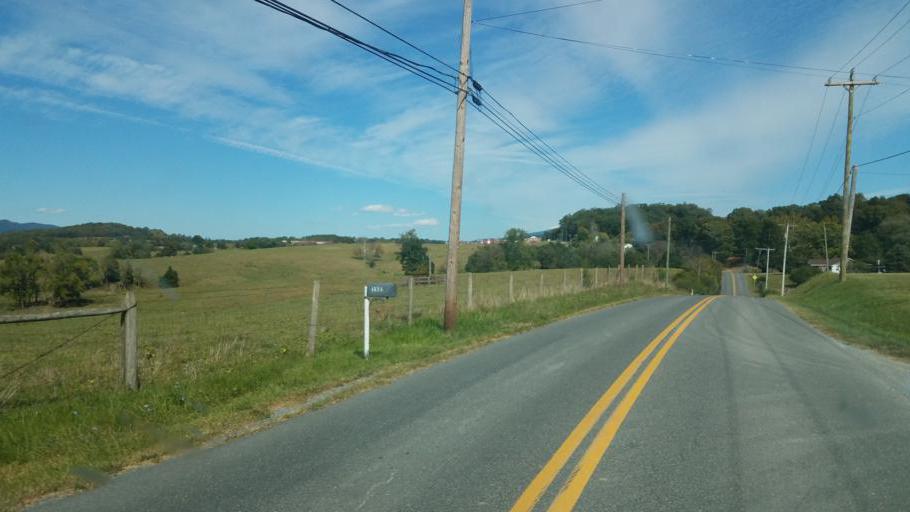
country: US
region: Virginia
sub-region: Page County
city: Luray
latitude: 38.6447
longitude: -78.4934
